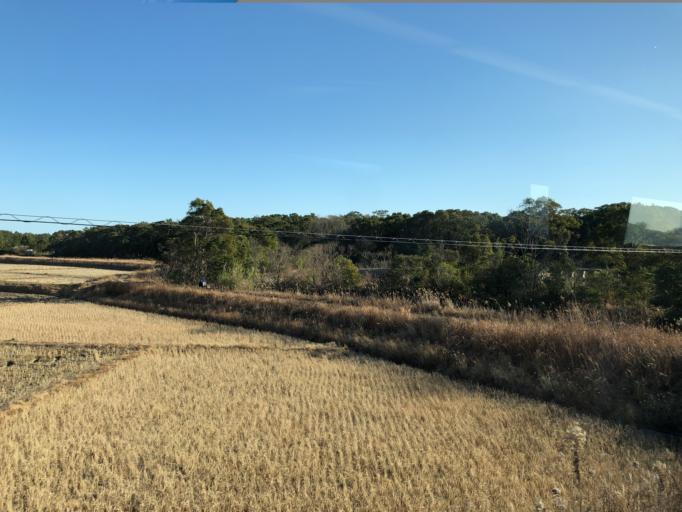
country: JP
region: Kochi
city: Nakamura
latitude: 33.0313
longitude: 133.0170
